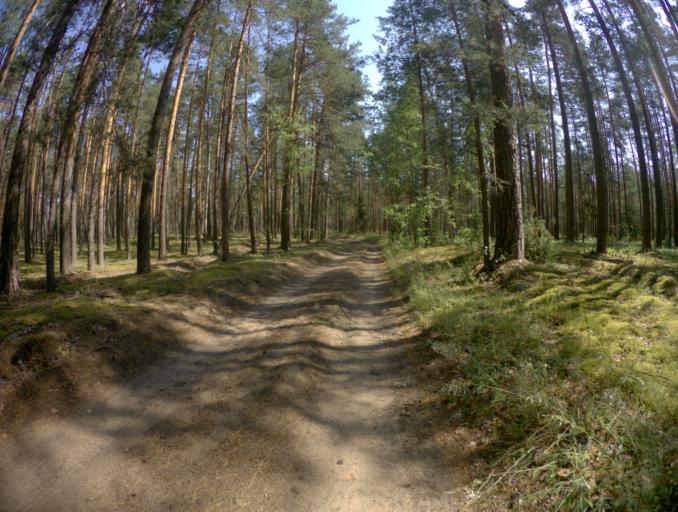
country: RU
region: Ivanovo
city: Talitsy
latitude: 56.3917
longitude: 42.2564
